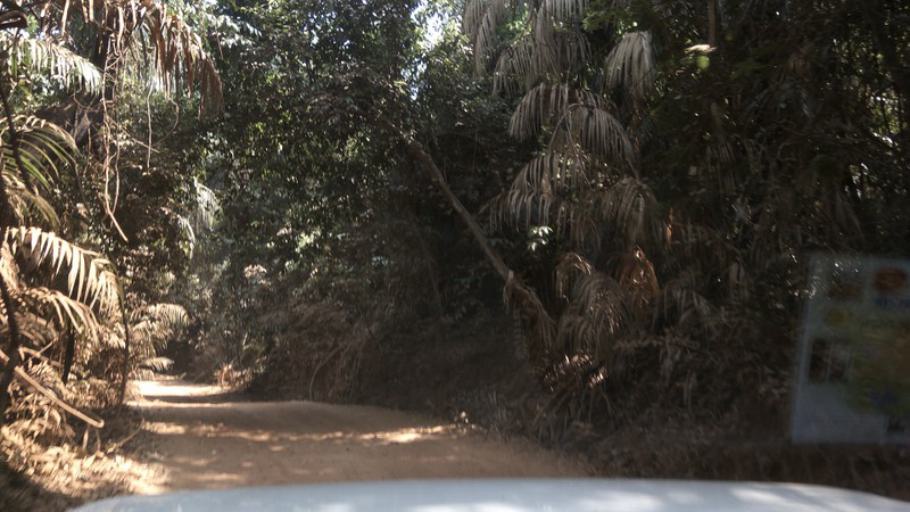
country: IN
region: Goa
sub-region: South Goa
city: Sanguem
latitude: 15.3112
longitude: 74.3018
